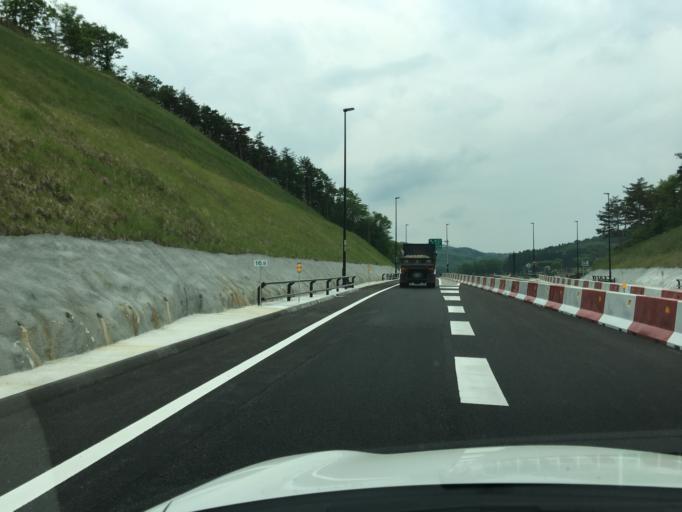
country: JP
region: Miyagi
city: Marumori
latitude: 37.7733
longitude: 140.7498
